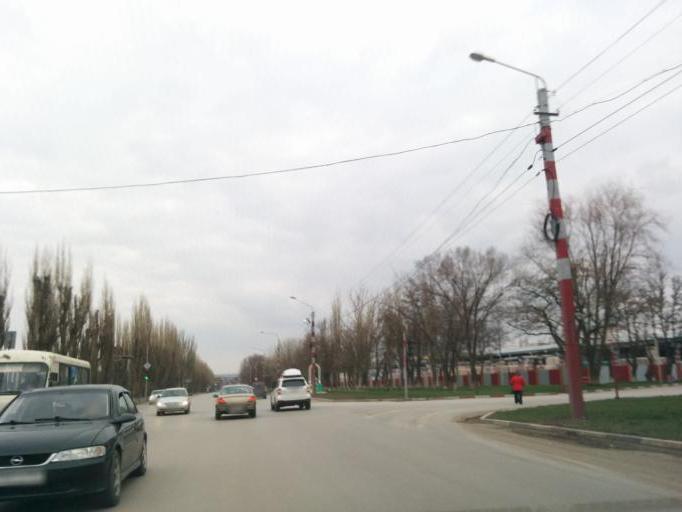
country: RU
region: Rostov
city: Novocherkassk
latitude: 47.4745
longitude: 40.1016
